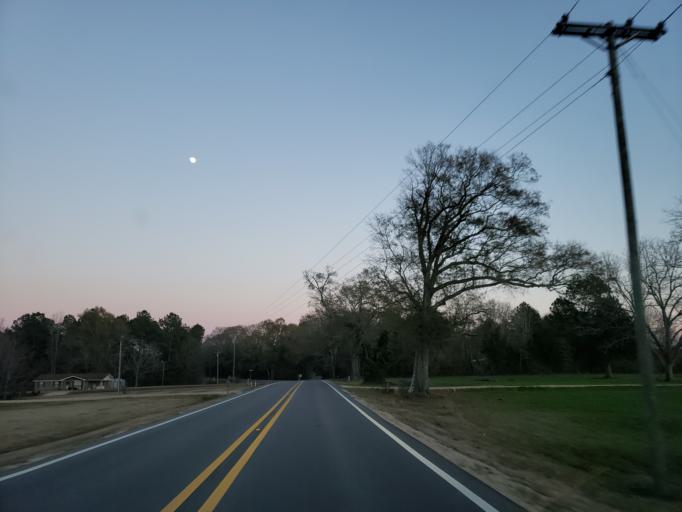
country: US
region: Mississippi
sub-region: Jones County
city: Ellisville
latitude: 31.5797
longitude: -89.2531
